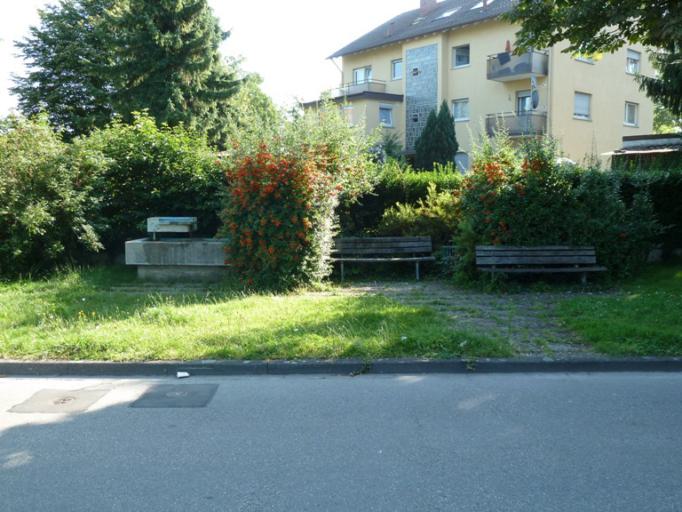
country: DE
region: Baden-Wuerttemberg
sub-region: Freiburg Region
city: Weil am Rhein
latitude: 47.6126
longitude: 7.6125
